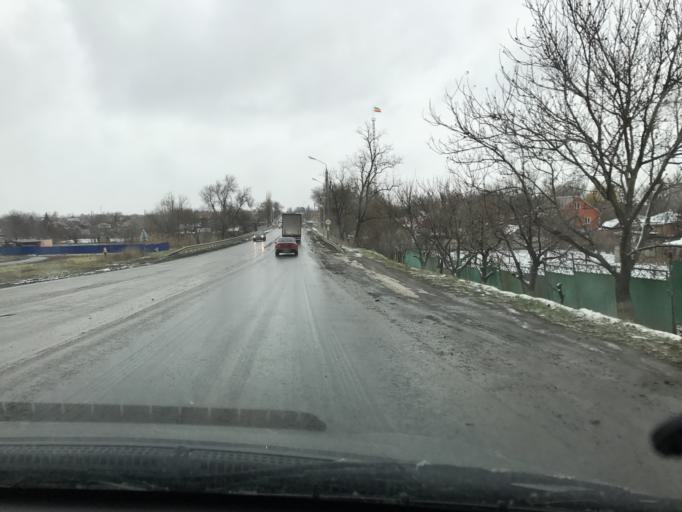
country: RU
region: Rostov
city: Kagal'nitskaya
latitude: 46.8863
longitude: 40.1429
